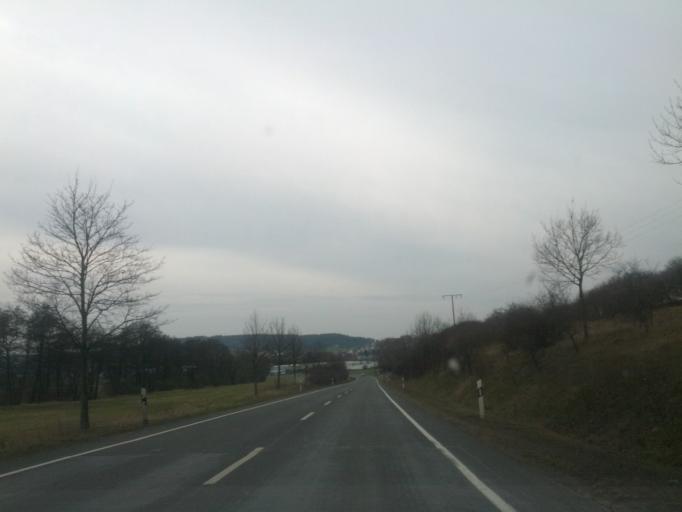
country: DE
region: Thuringia
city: Eisenach
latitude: 50.9983
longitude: 10.3350
